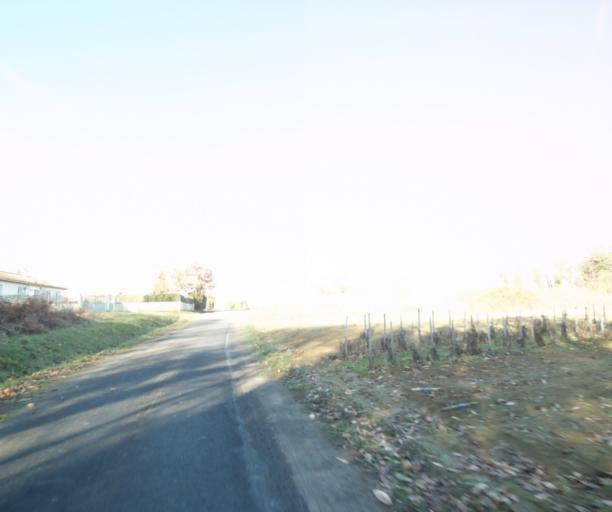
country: FR
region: Poitou-Charentes
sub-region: Departement de la Charente-Maritime
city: Burie
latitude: 45.7773
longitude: -0.4325
